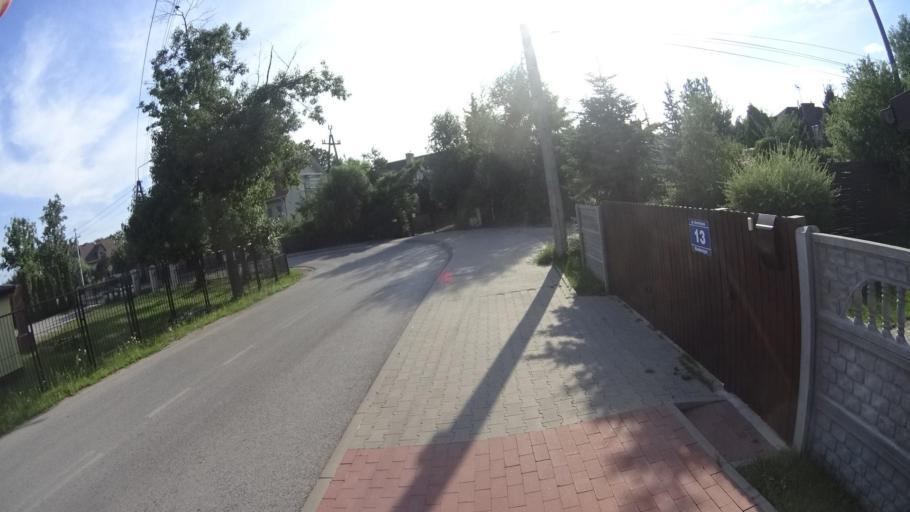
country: PL
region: Masovian Voivodeship
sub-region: Powiat pruszkowski
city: Nadarzyn
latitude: 52.0923
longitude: 20.7994
